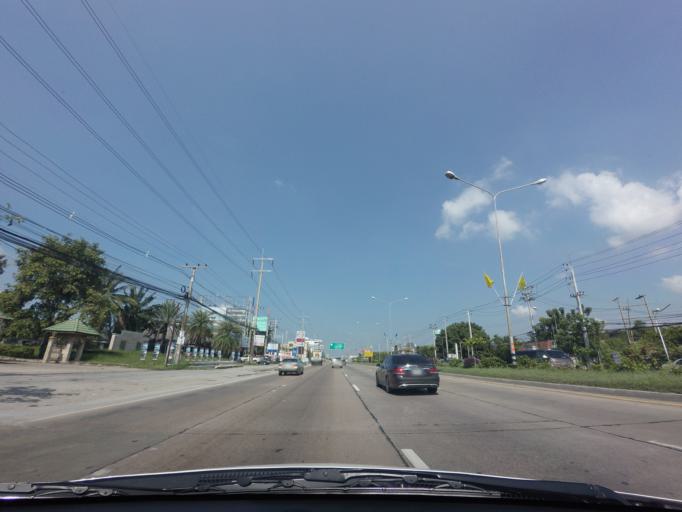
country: TH
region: Nakhon Pathom
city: Nakhon Chai Si
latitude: 13.7770
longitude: 100.1781
